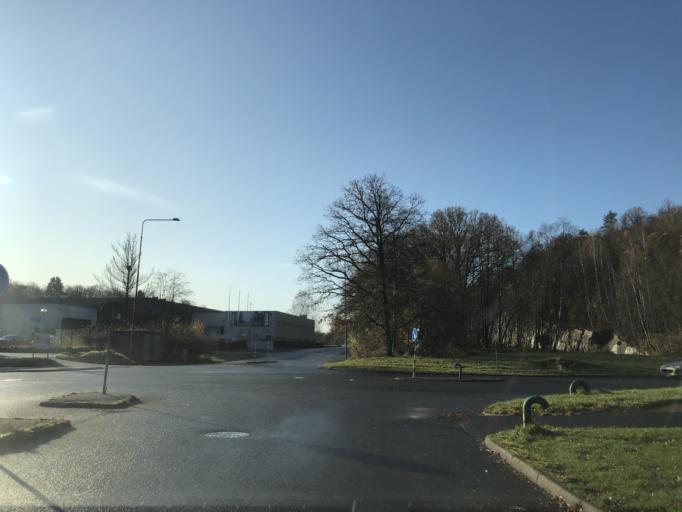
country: SE
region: Vaestra Goetaland
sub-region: Goteborg
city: Gardsten
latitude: 57.8007
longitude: 12.0434
